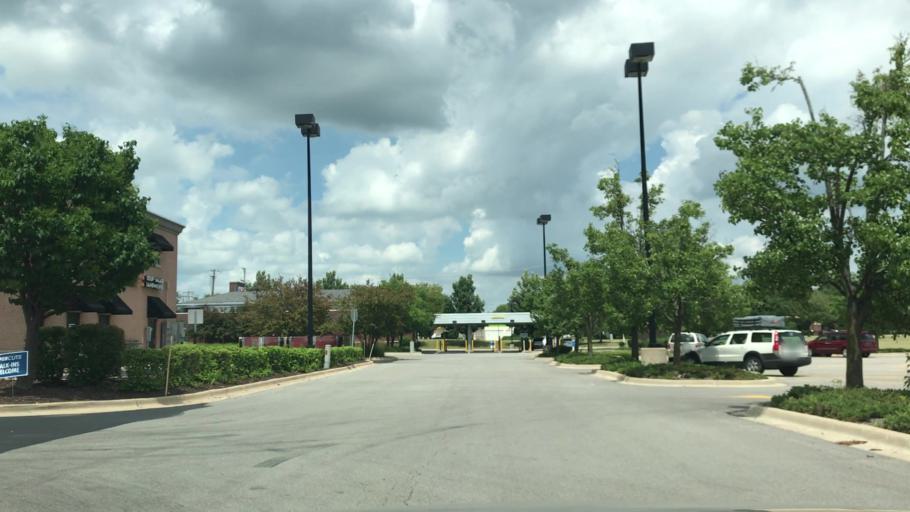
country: US
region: Illinois
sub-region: DuPage County
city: Warrenville
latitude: 41.7801
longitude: -88.2398
